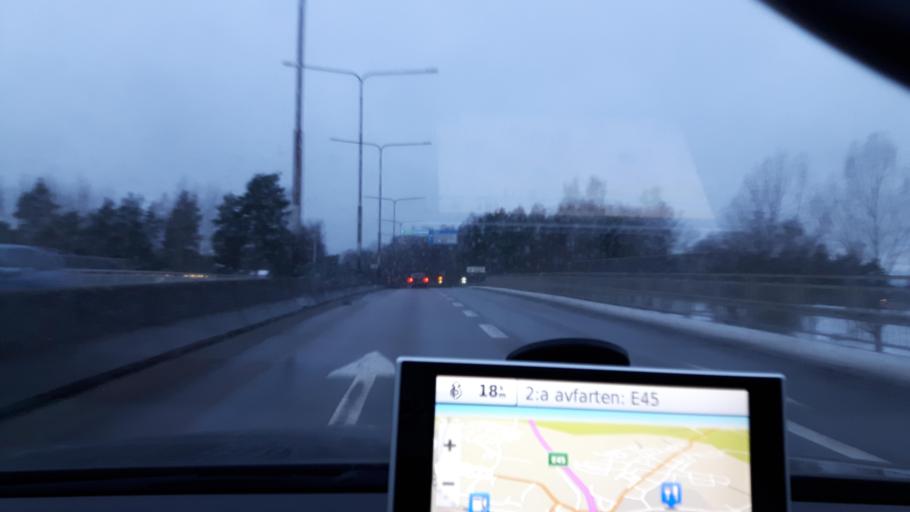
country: SE
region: Vaermland
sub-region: Saffle Kommun
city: Saeffle
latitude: 59.1357
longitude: 12.9182
